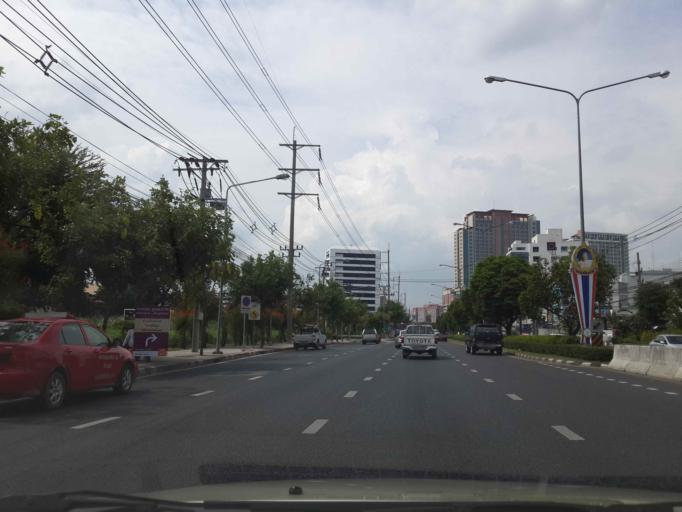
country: TH
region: Bangkok
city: Bang Kapi
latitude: 13.7491
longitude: 100.6443
